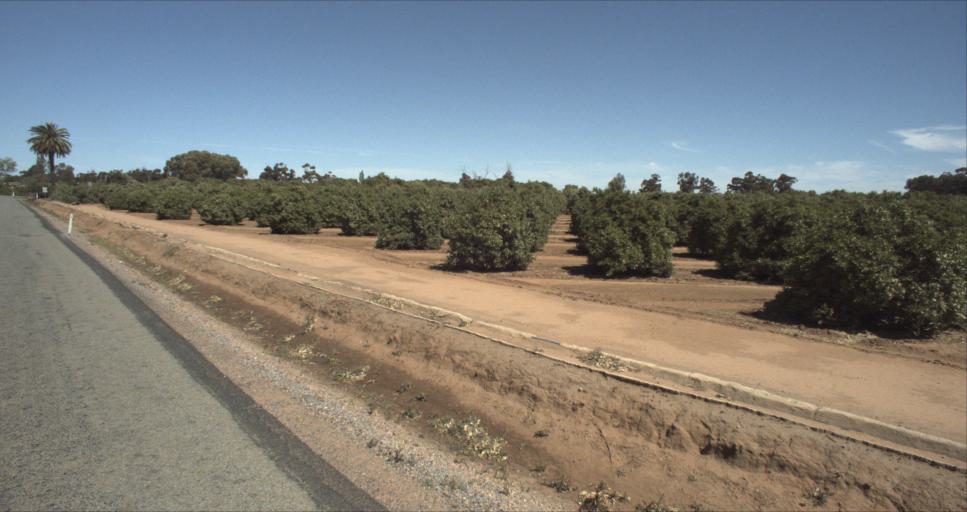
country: AU
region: New South Wales
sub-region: Leeton
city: Leeton
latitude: -34.5475
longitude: 146.3701
